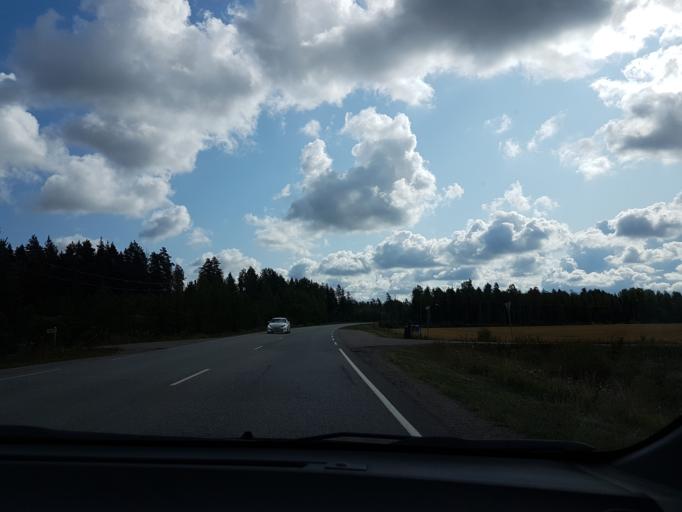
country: FI
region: Uusimaa
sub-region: Helsinki
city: Nickby
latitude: 60.4703
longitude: 25.2613
